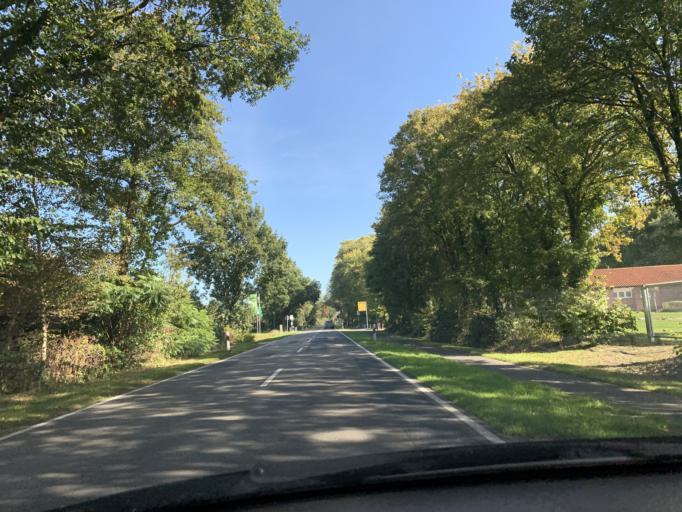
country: DE
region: Lower Saxony
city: Apen
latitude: 53.2178
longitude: 7.7848
